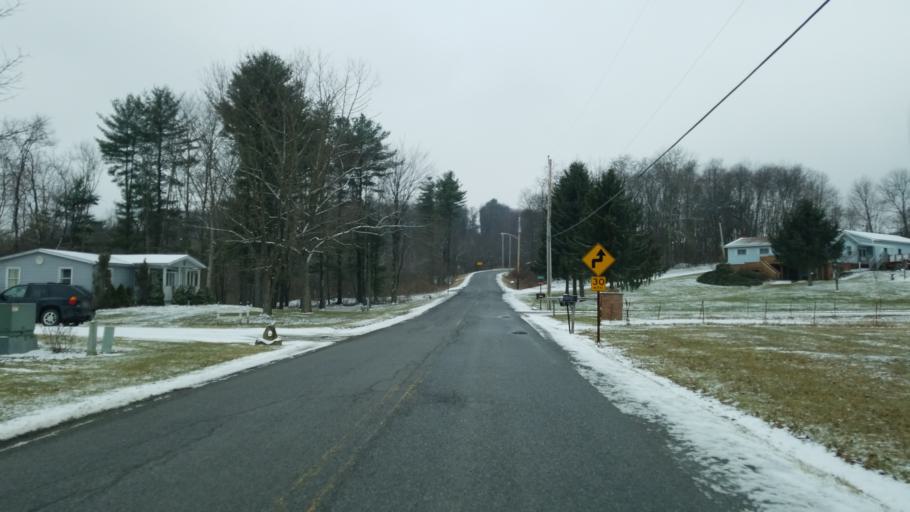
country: US
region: Pennsylvania
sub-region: Clearfield County
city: Sandy
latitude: 41.0785
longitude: -78.7939
